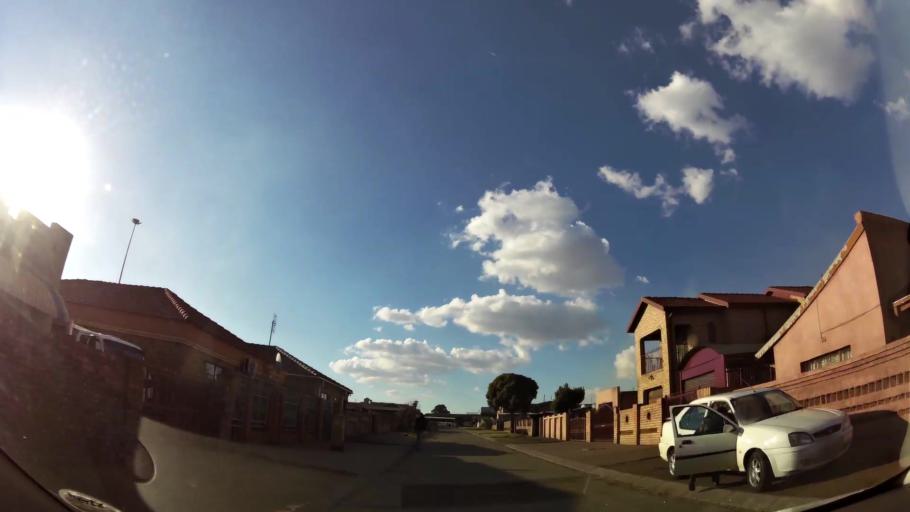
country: ZA
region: Mpumalanga
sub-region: Nkangala District Municipality
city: Witbank
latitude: -25.8679
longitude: 29.1730
